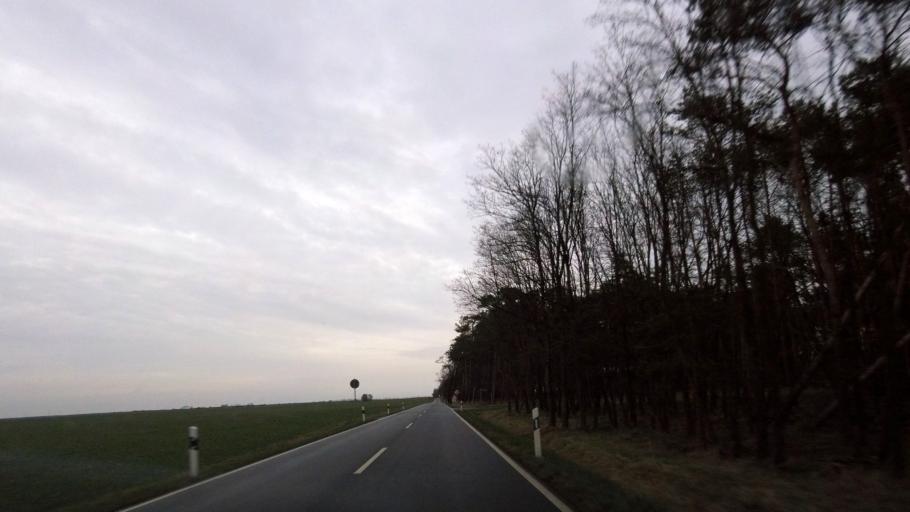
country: DE
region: Brandenburg
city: Niedergorsdorf
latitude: 51.9321
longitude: 12.9685
